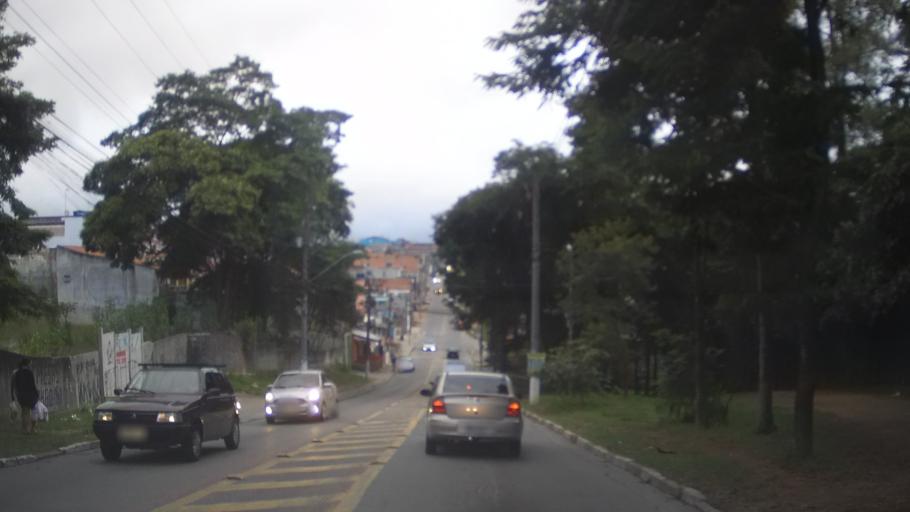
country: BR
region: Sao Paulo
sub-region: Itaquaquecetuba
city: Itaquaquecetuba
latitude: -23.4506
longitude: -46.4238
